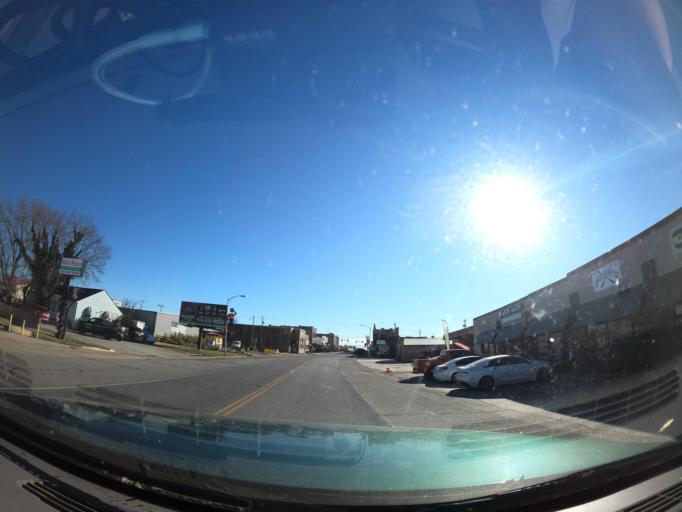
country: US
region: Oklahoma
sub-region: McIntosh County
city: Eufaula
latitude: 35.2889
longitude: -95.5824
